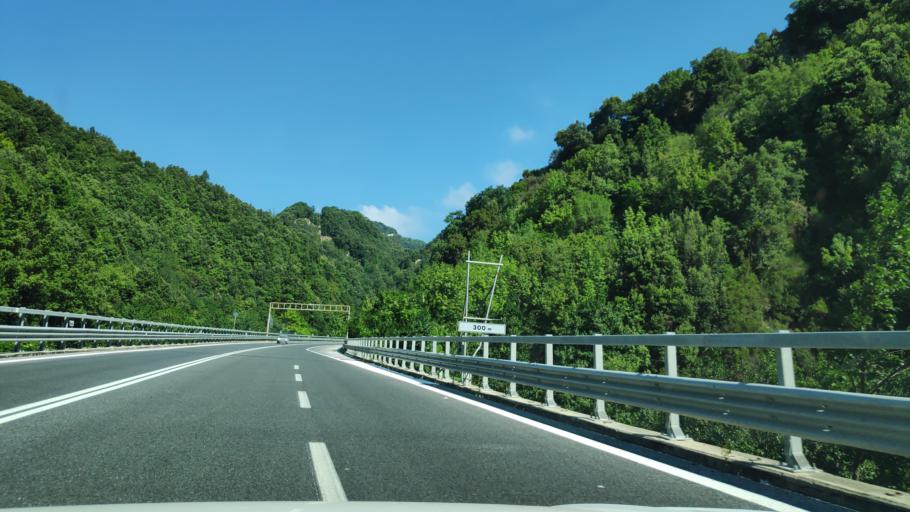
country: IT
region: Calabria
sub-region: Provincia di Reggio Calabria
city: Amato
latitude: 38.3727
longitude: 16.1797
